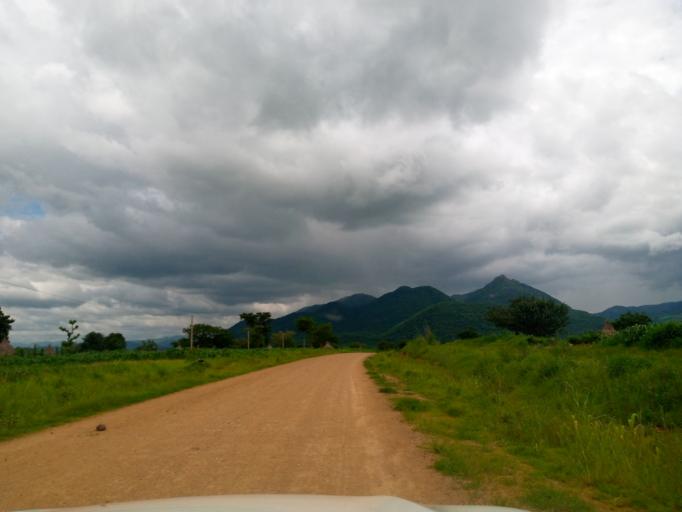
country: ET
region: Oromiya
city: Mendi
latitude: 10.1849
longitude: 35.0931
